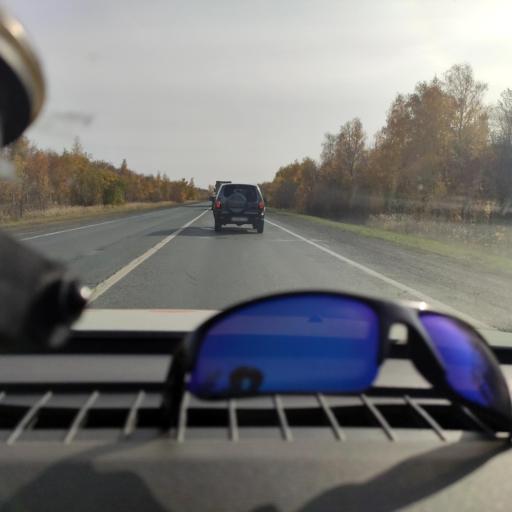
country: RU
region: Samara
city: Chapayevsk
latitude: 52.9954
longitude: 49.8079
